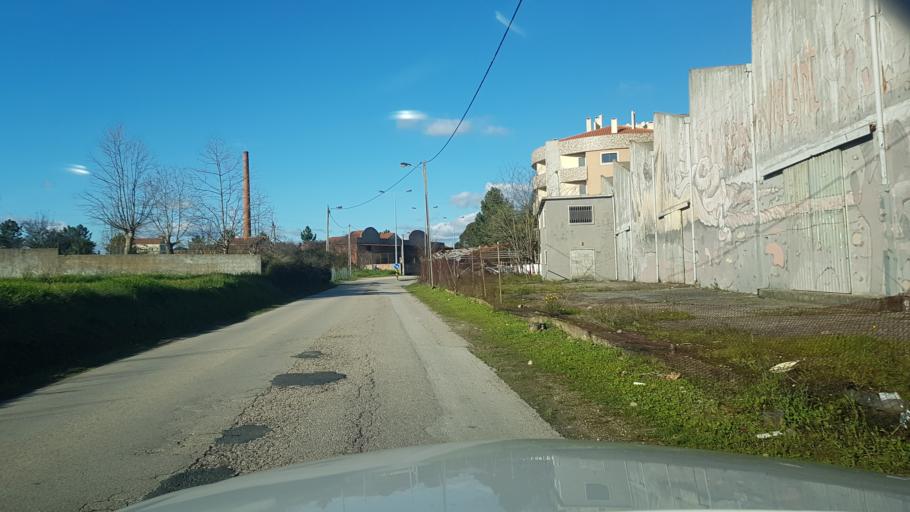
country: PT
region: Santarem
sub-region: Entroncamento
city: Entroncamento
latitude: 39.4767
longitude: -8.4736
